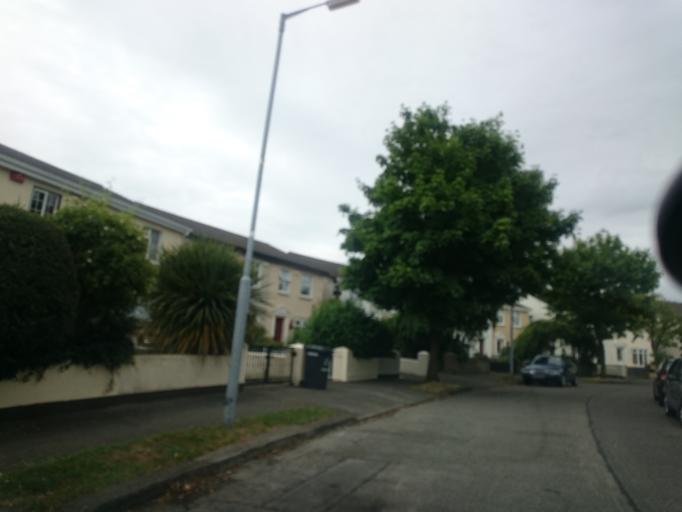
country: IE
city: Greenhills
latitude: 53.3154
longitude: -6.3057
